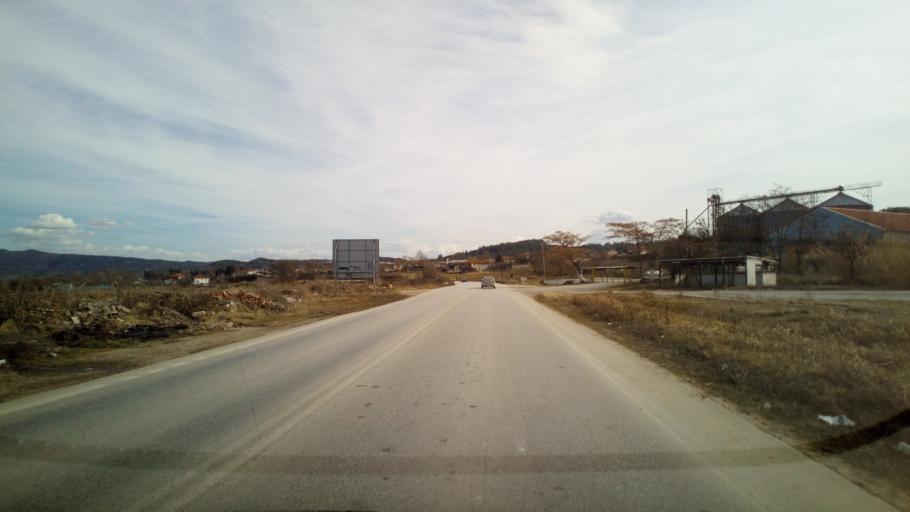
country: GR
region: Central Macedonia
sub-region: Nomos Thessalonikis
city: Gerakarou
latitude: 40.6335
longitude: 23.1987
